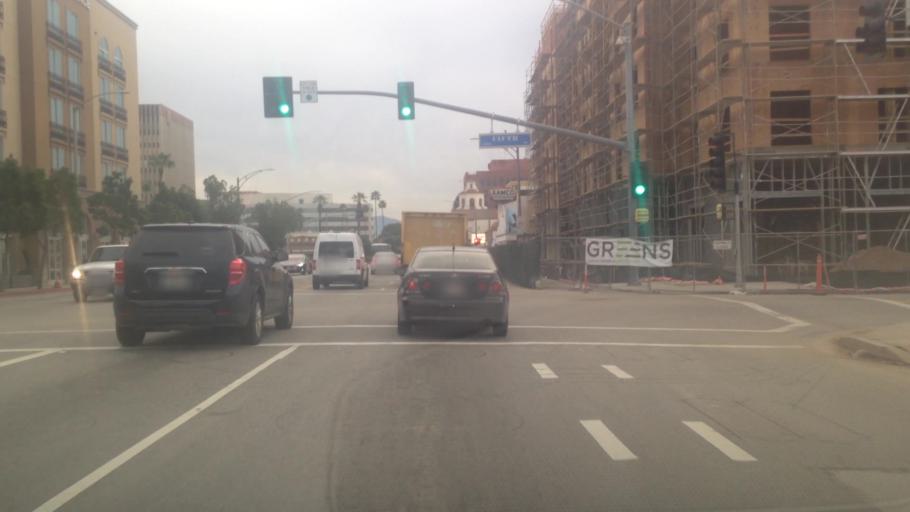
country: US
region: California
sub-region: Riverside County
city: Rubidoux
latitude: 33.9857
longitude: -117.3737
